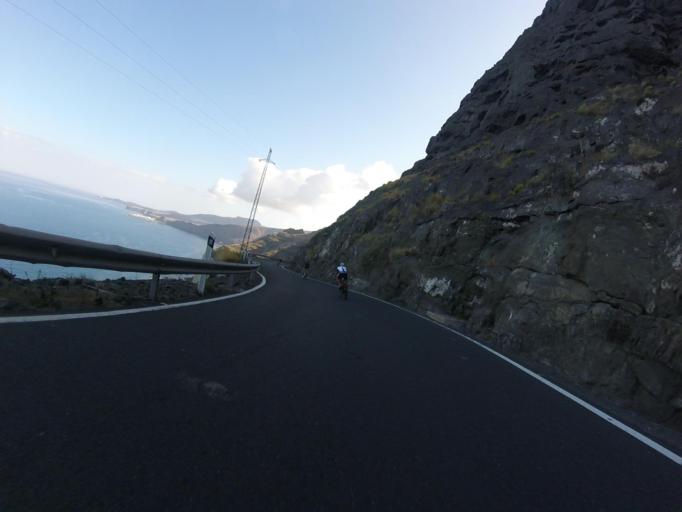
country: ES
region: Canary Islands
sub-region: Provincia de Las Palmas
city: Agaete
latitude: 28.0682
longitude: -15.7217
